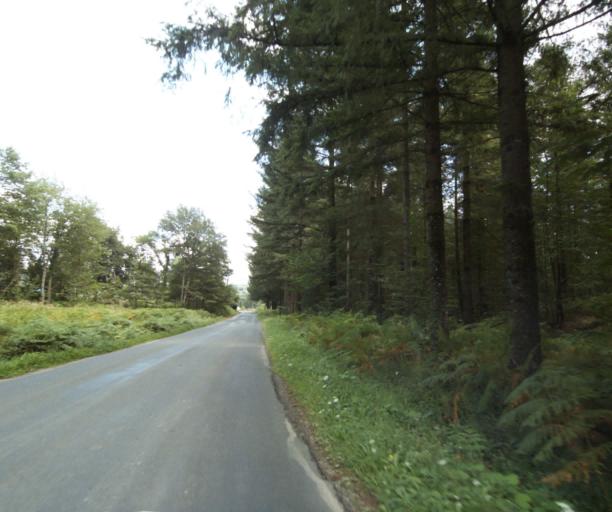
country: FR
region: Limousin
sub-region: Departement de la Correze
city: Sainte-Fortunade
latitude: 45.1962
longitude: 1.8169
